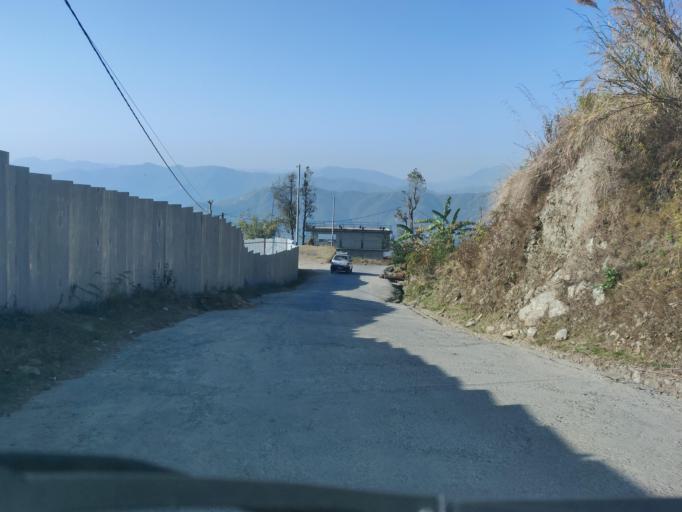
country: NP
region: Western Region
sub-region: Gandaki Zone
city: Pokhara
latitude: 28.2437
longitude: 83.9499
